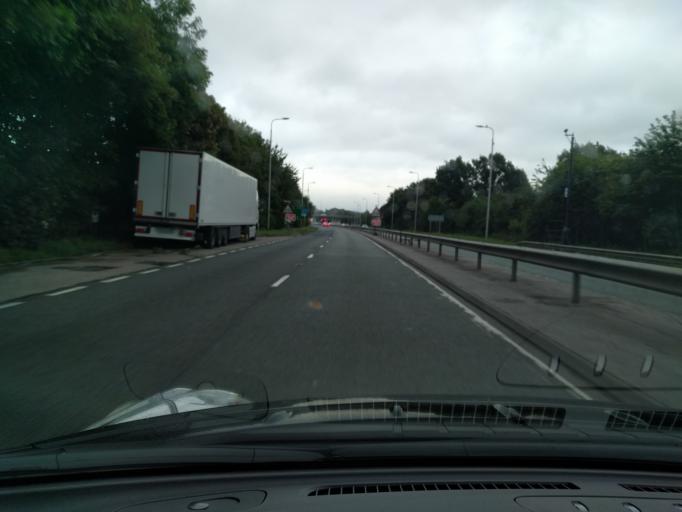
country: GB
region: England
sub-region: Borough of Wigan
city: Ashton in Makerfield
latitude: 53.4714
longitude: -2.6398
